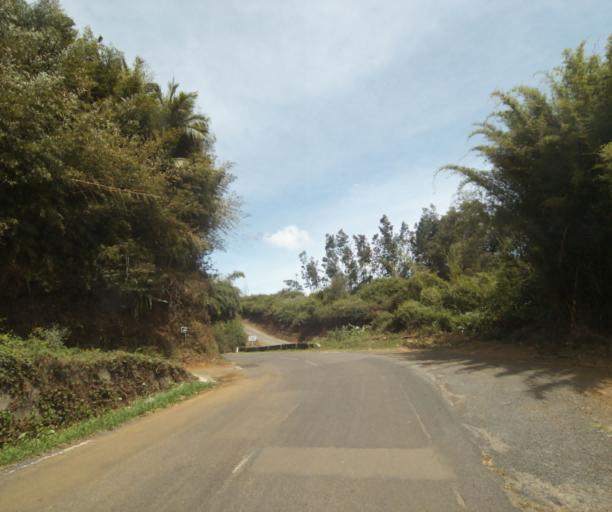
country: RE
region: Reunion
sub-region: Reunion
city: Trois-Bassins
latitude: -21.0672
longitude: 55.3091
